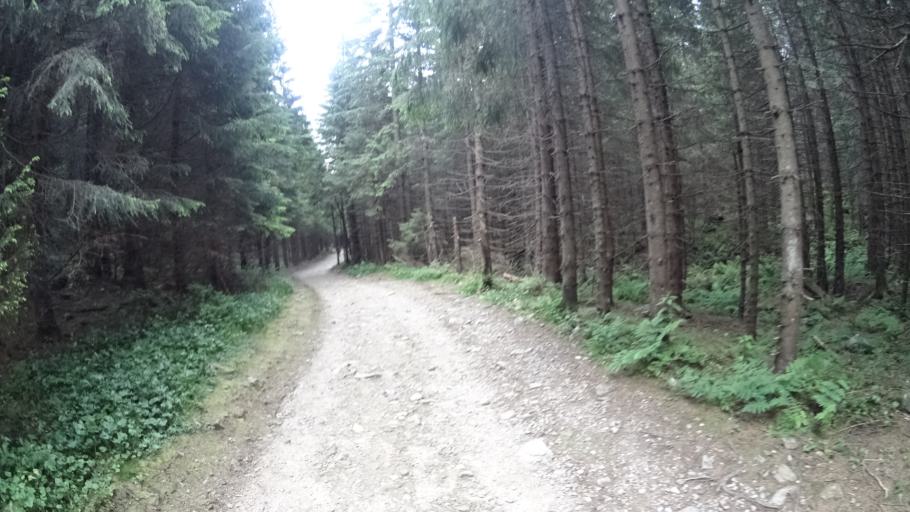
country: PL
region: Lesser Poland Voivodeship
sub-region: Powiat tatrzanski
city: Zakopane
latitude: 49.2512
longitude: 19.9588
